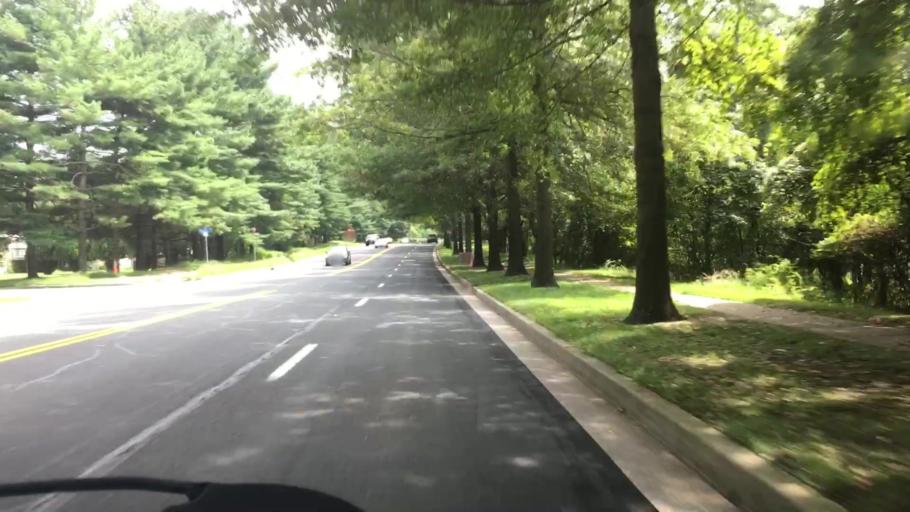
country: US
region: Maryland
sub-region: Howard County
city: Columbia
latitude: 39.1935
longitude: -76.8335
